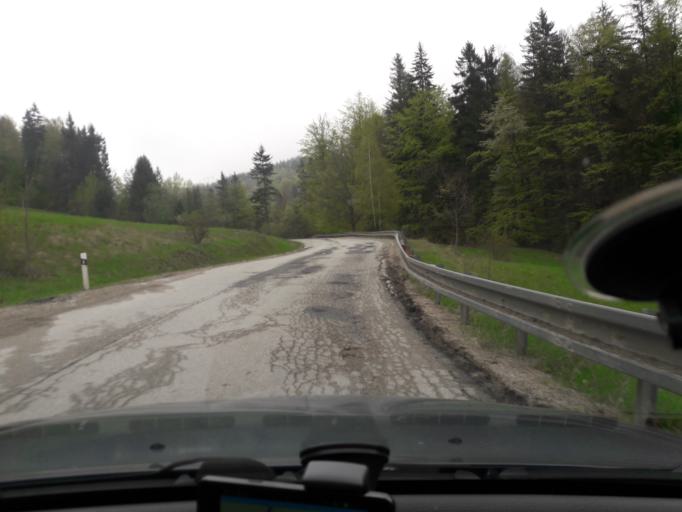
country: SK
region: Banskobystricky
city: Revuca
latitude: 48.7817
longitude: 20.1189
